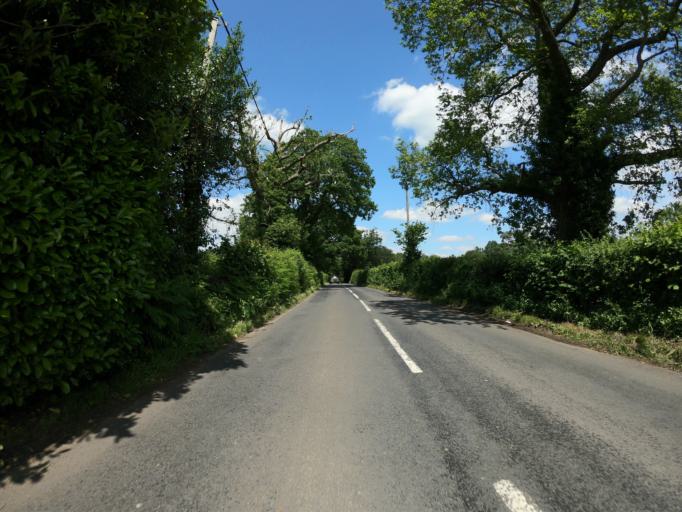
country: GB
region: England
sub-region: Kent
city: Halstead
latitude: 51.3208
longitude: 0.1284
